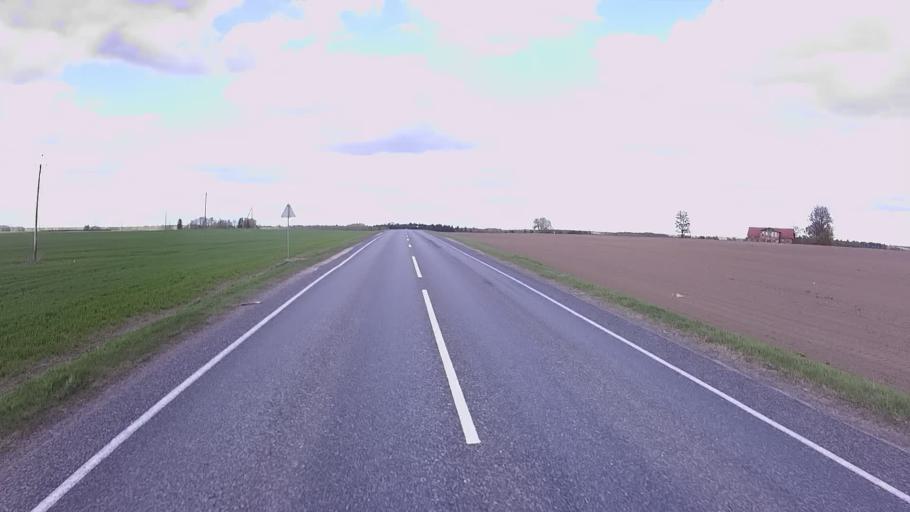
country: EE
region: Jogevamaa
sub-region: Jogeva linn
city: Jogeva
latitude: 58.7951
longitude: 26.4837
